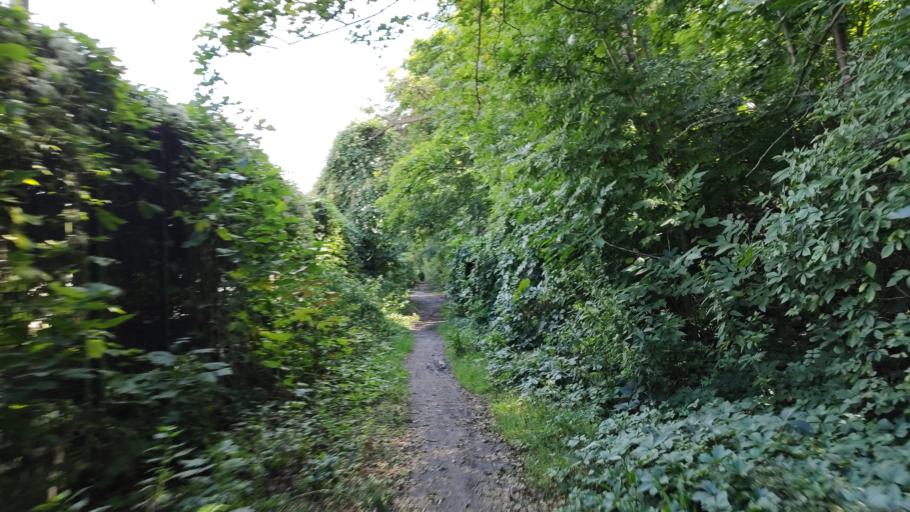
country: PL
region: Lower Silesian Voivodeship
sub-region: Powiat wroclawski
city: Wroclaw
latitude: 51.0803
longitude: 17.0005
